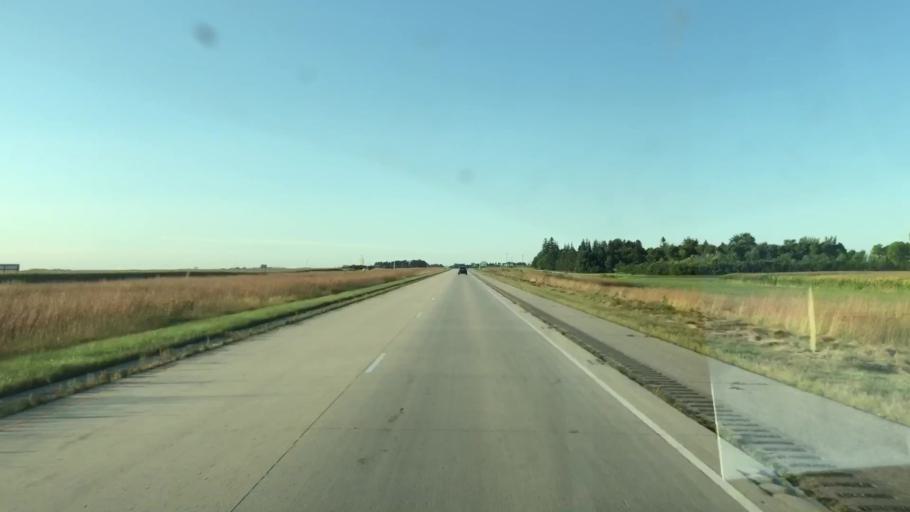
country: US
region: Iowa
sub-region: Osceola County
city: Sibley
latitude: 43.5060
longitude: -95.6835
